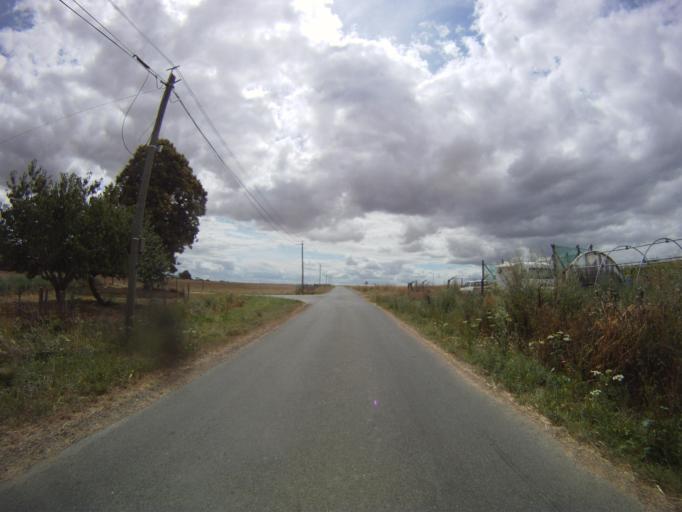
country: FR
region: Centre
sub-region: Departement du Loir-et-Cher
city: Montoire-sur-le-Loir
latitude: 47.6896
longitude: 0.7923
